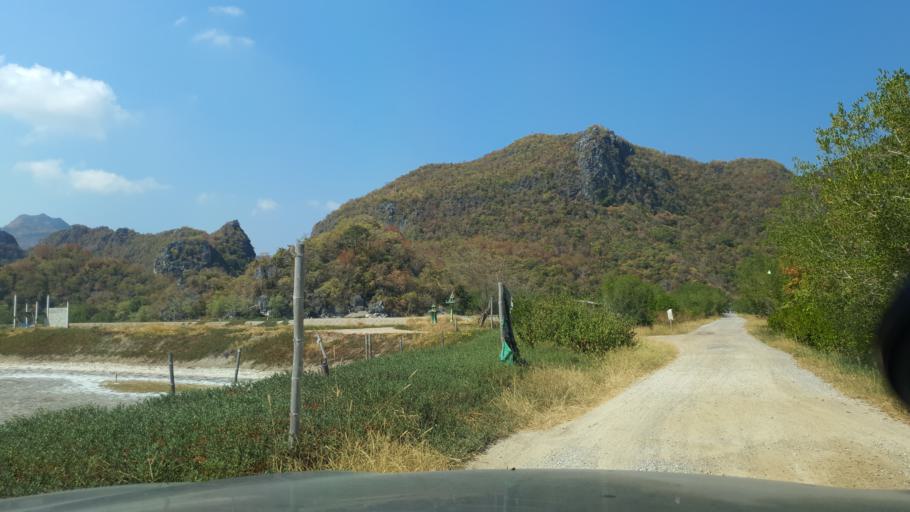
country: TH
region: Prachuap Khiri Khan
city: Sam Roi Yot
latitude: 12.1997
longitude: 99.9936
